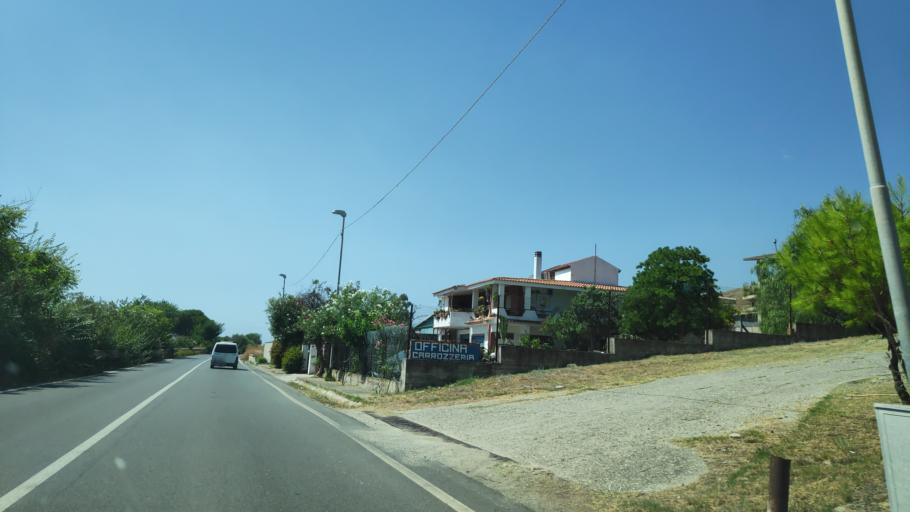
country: IT
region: Calabria
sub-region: Provincia di Reggio Calabria
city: Brancaleone-Marina
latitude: 37.9786
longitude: 16.1132
